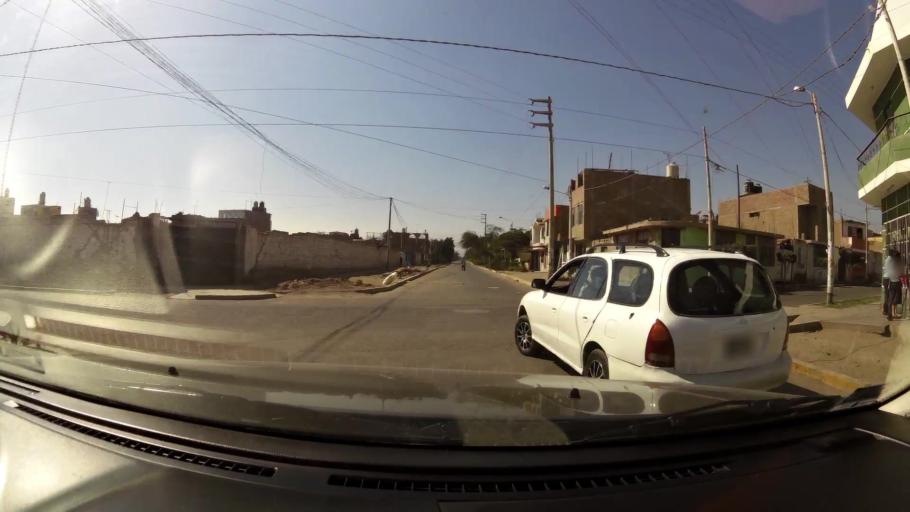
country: PE
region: Ica
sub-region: Provincia de Ica
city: La Tinguina
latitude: -14.0367
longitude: -75.7100
